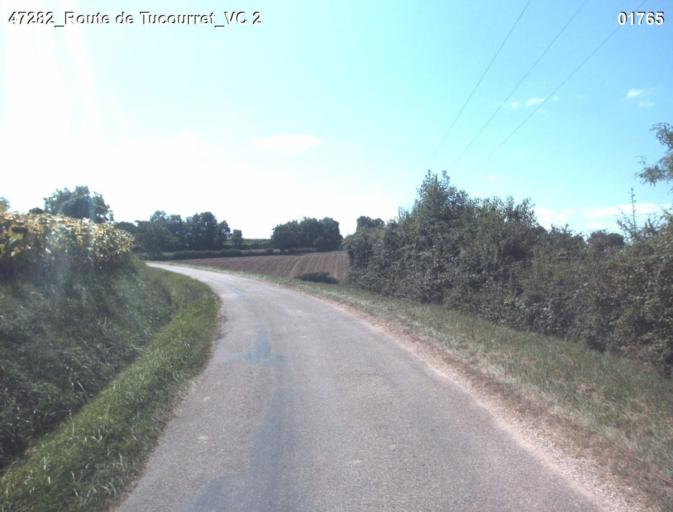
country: FR
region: Aquitaine
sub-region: Departement du Lot-et-Garonne
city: Laplume
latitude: 44.1041
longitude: 0.4881
